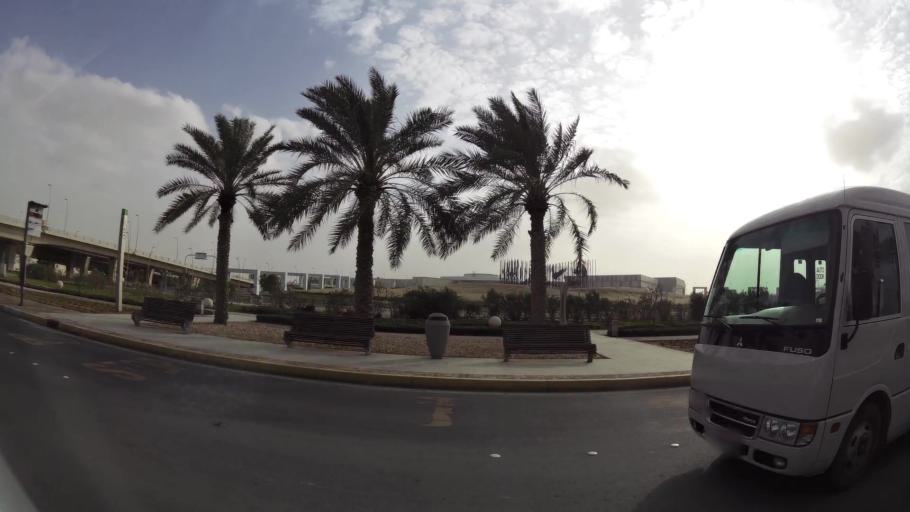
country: AE
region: Abu Dhabi
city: Abu Dhabi
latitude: 24.4936
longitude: 54.6114
